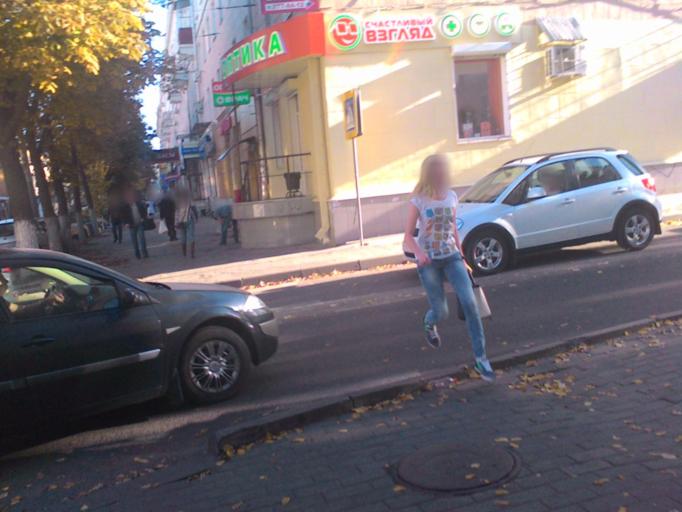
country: RU
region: Voronezj
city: Voronezh
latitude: 51.6700
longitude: 39.1897
